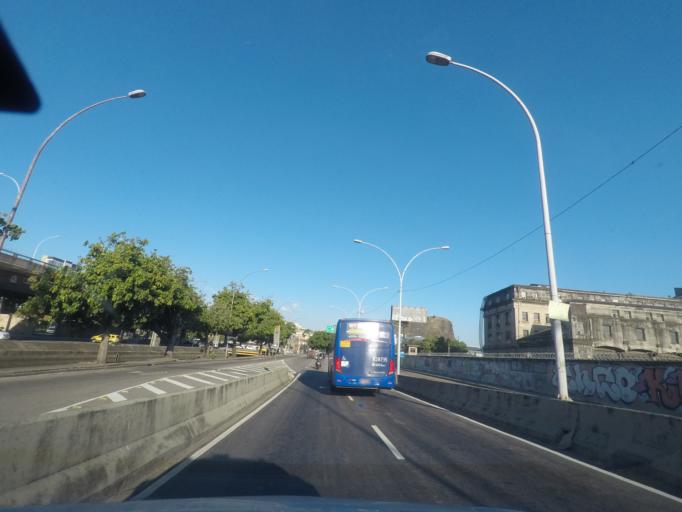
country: BR
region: Rio de Janeiro
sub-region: Rio De Janeiro
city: Rio de Janeiro
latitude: -22.9070
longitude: -43.2115
